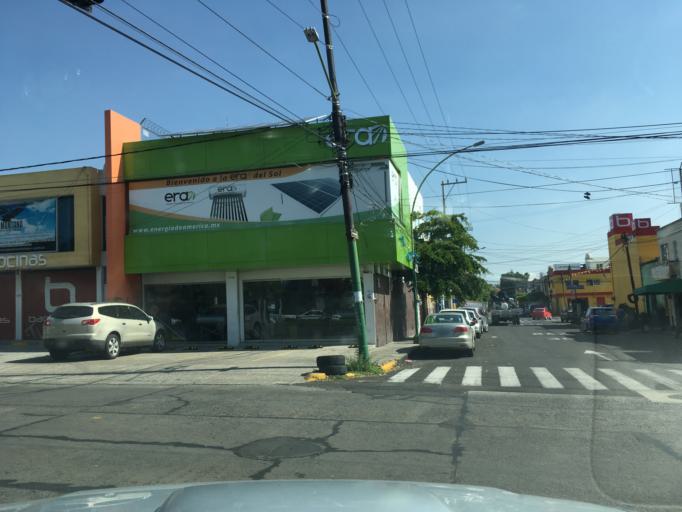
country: MX
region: Jalisco
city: Guadalajara
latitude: 20.6669
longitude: -103.3634
